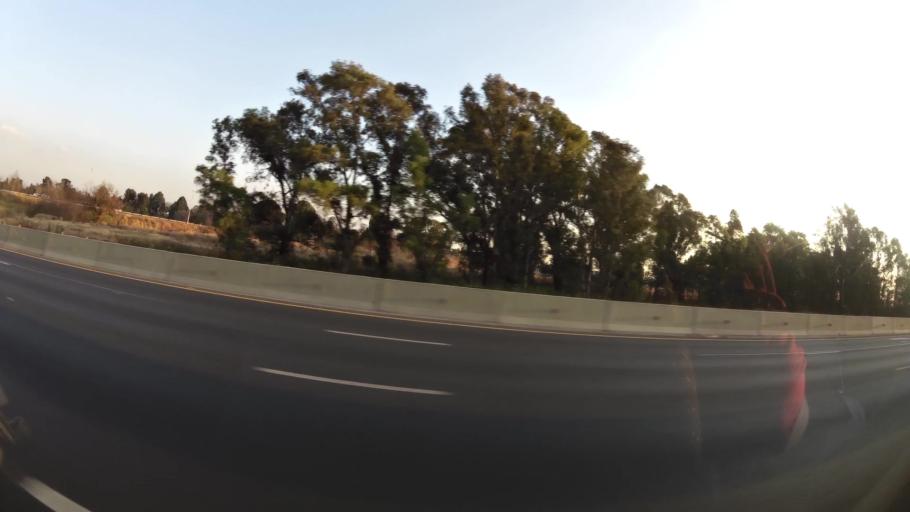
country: ZA
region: Gauteng
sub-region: Ekurhuleni Metropolitan Municipality
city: Benoni
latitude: -26.1764
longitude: 28.2917
